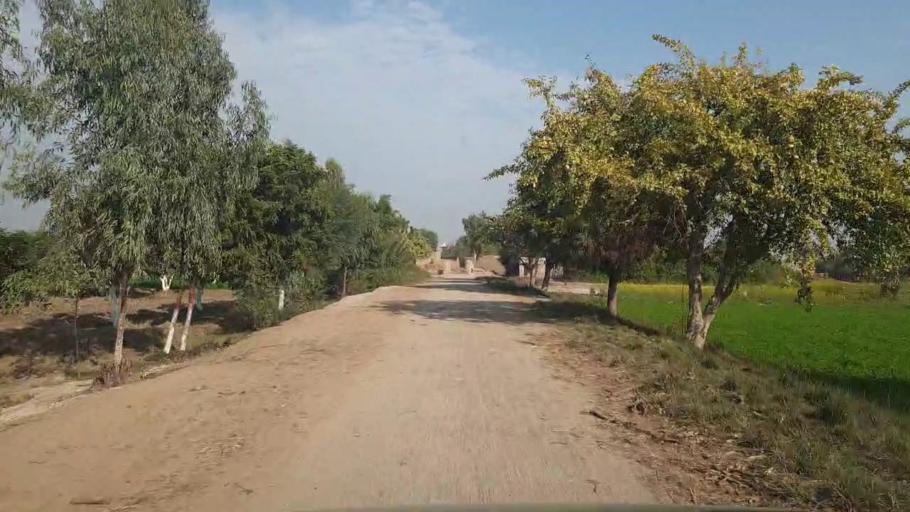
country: PK
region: Sindh
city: Tando Adam
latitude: 25.7602
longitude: 68.5882
